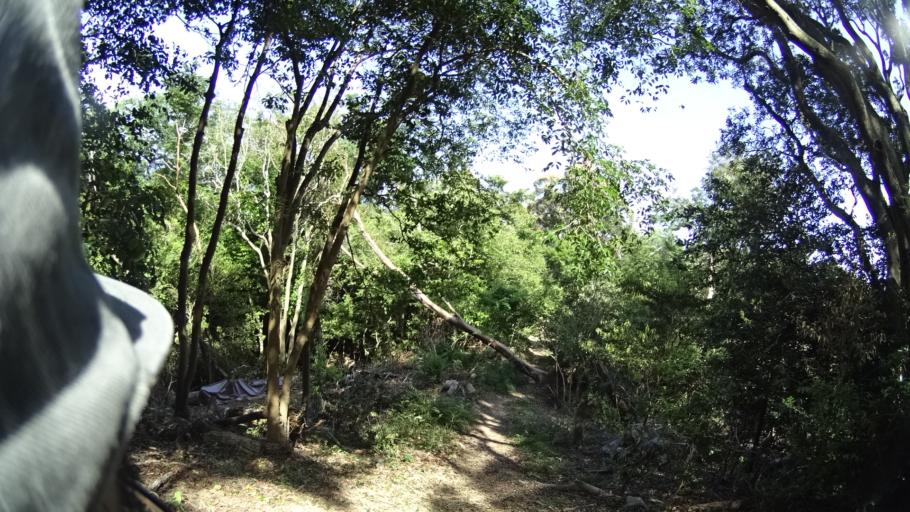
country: JP
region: Shizuoka
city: Kosai-shi
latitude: 34.7818
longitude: 137.4977
